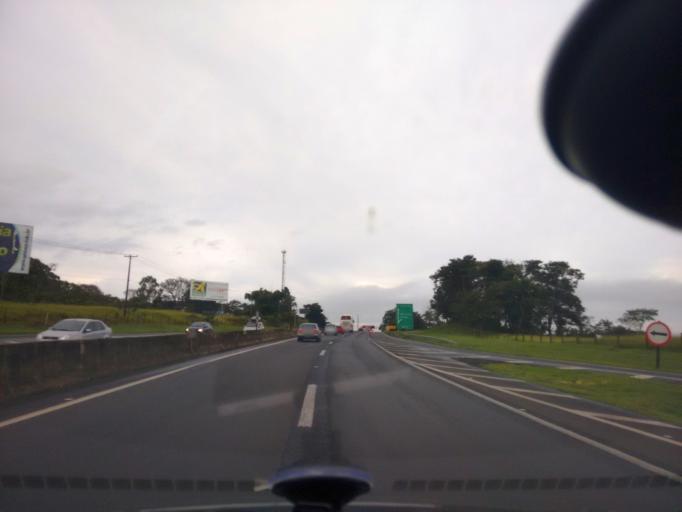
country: BR
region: Sao Paulo
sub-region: Sao Carlos
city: Sao Carlos
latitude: -22.0422
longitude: -47.8620
